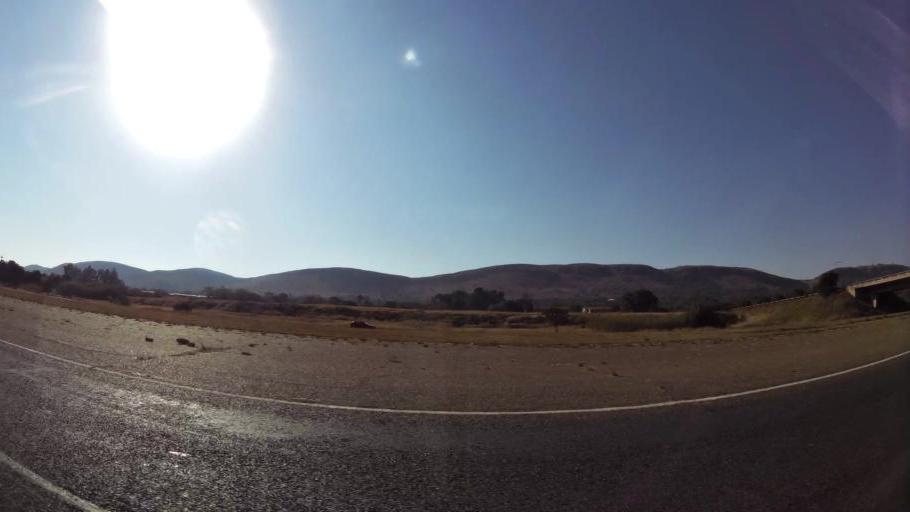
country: ZA
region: Gauteng
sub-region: City of Tshwane Metropolitan Municipality
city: Pretoria
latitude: -25.7045
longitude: 28.1459
